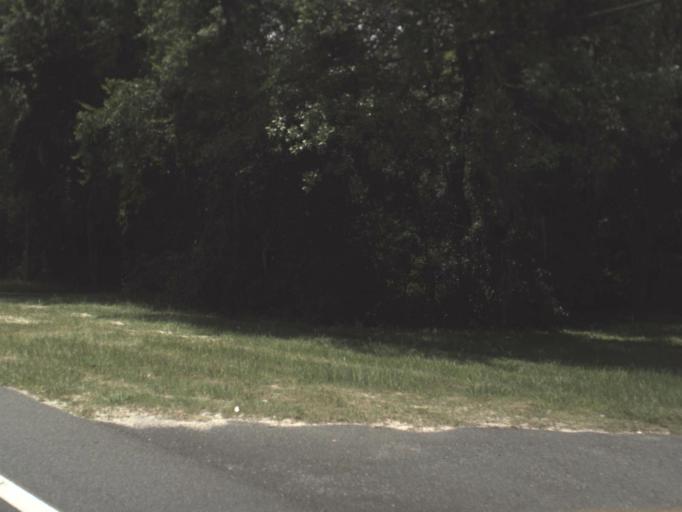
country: US
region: Florida
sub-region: Clay County
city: Keystone Heights
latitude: 29.7678
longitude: -82.0081
